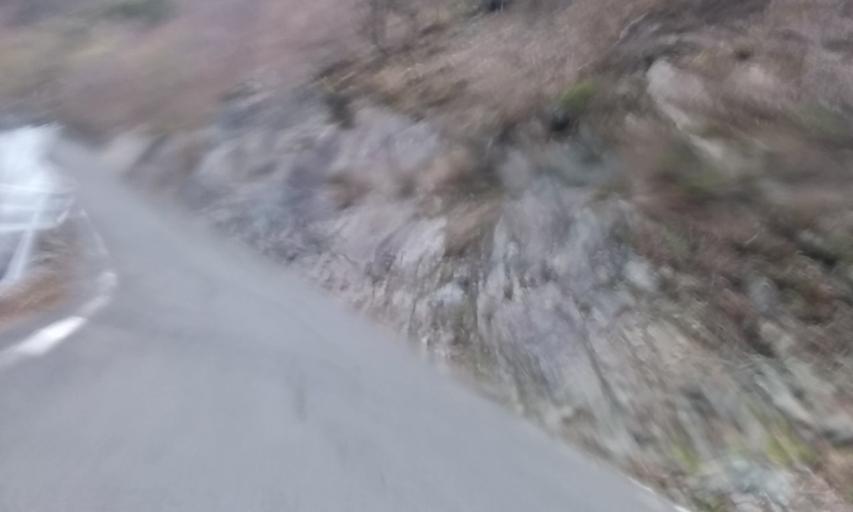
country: JP
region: Ehime
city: Saijo
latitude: 33.7930
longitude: 133.2039
